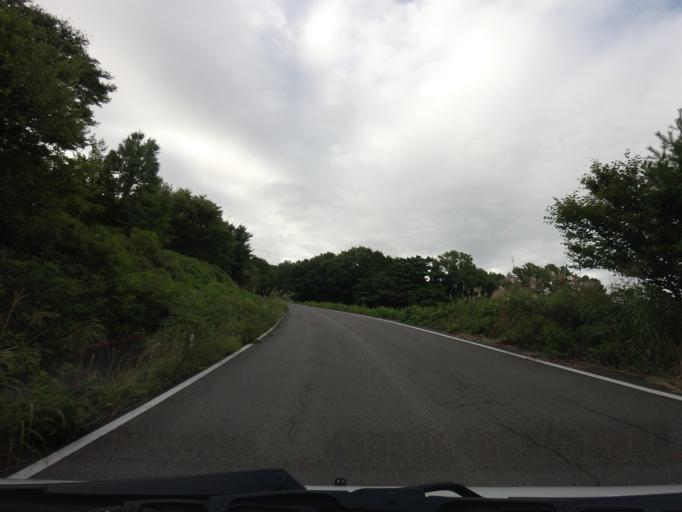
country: JP
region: Fukushima
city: Nihommatsu
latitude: 37.6136
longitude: 140.3437
